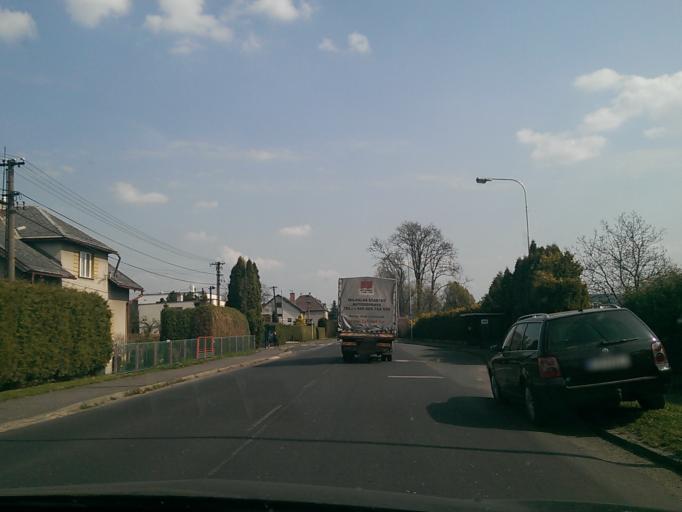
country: CZ
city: Ohrazenice
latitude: 50.5940
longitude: 15.1253
